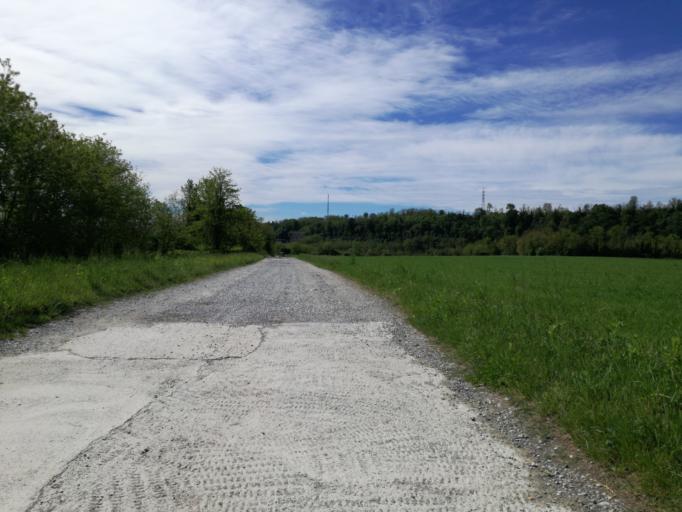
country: IT
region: Lombardy
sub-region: Provincia di Monza e Brianza
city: Porto d'Adda
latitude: 45.6614
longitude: 9.4836
